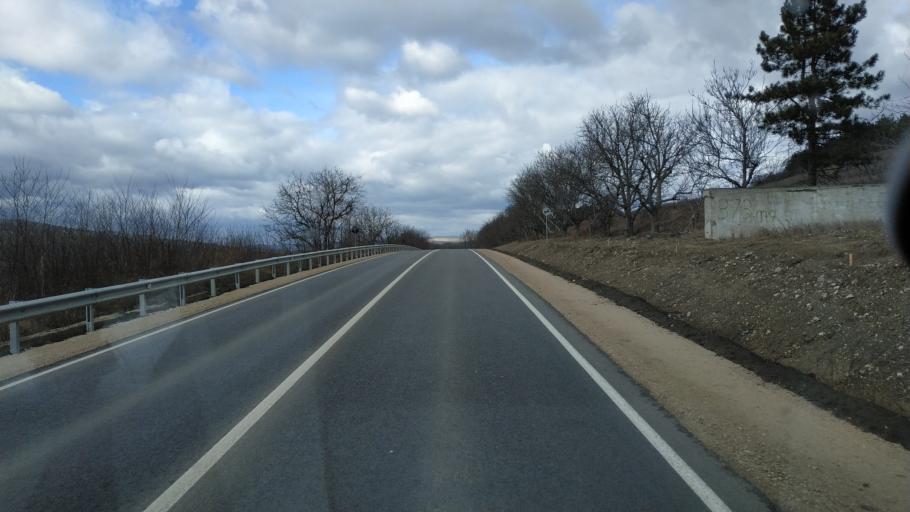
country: MD
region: Stinga Nistrului
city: Bucovat
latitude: 47.1937
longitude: 28.4385
